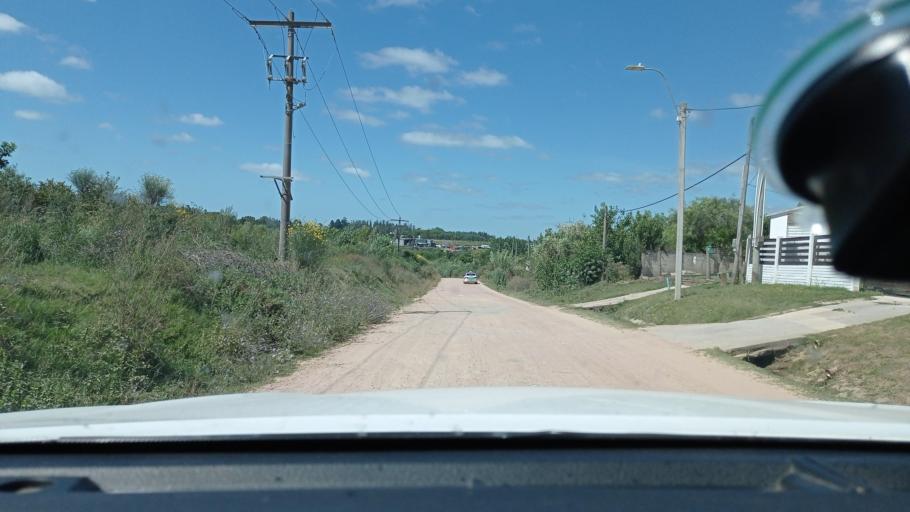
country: UY
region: Canelones
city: Pando
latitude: -34.7215
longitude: -55.9725
